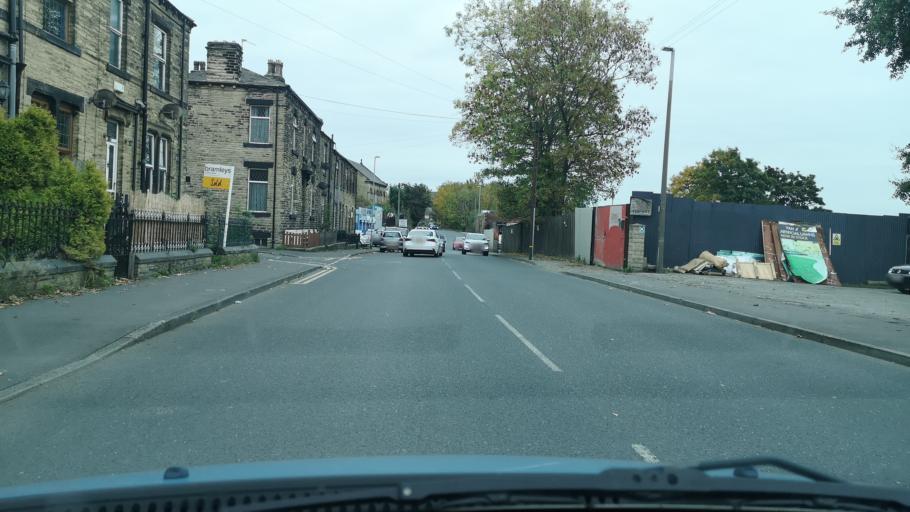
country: GB
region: England
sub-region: Kirklees
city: Heckmondwike
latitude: 53.7048
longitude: -1.6730
